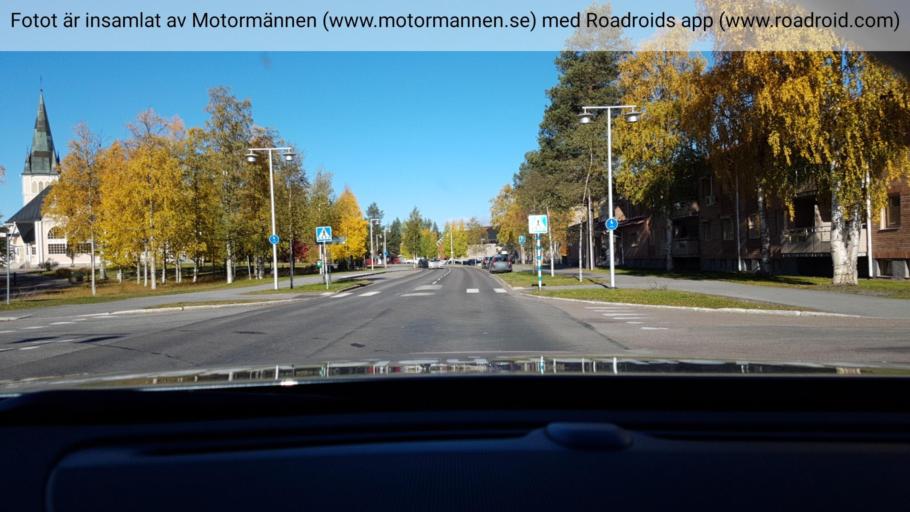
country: SE
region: Norrbotten
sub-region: Arvidsjaurs Kommun
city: Arvidsjaur
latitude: 65.5948
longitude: 19.1697
